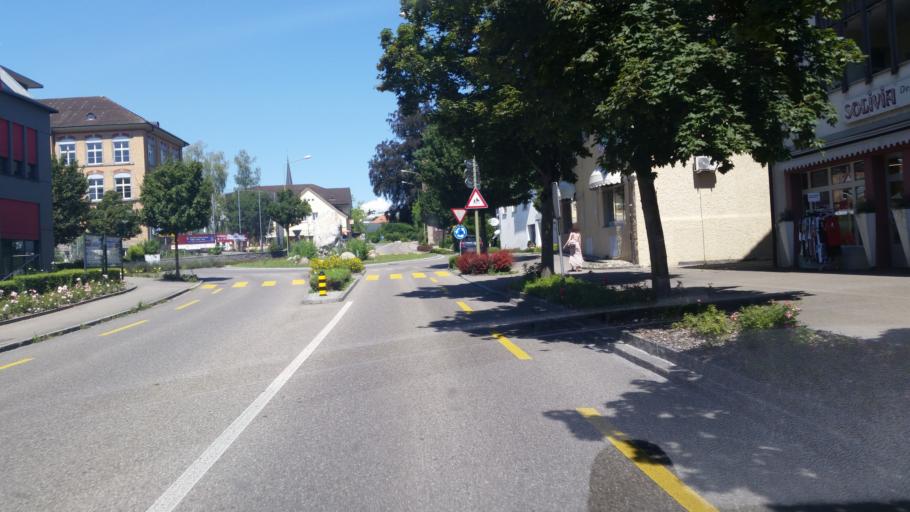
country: CH
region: Zurich
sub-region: Bezirk Buelach
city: Bulach
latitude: 47.5178
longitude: 8.5386
